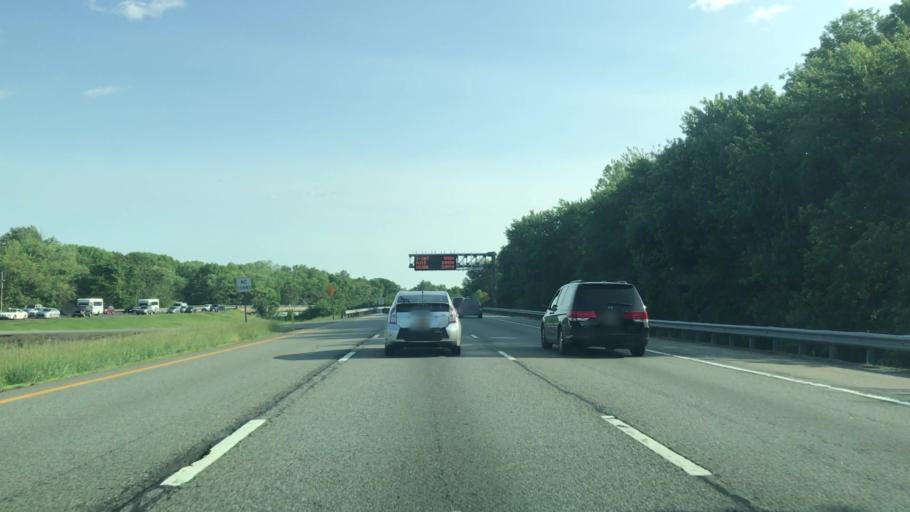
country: US
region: New Jersey
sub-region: Essex County
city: Fairfield
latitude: 40.8699
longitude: -74.3305
